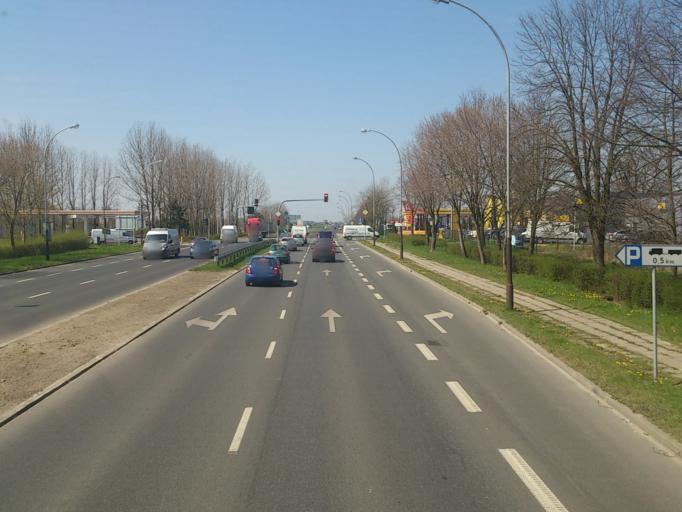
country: PL
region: Lodz Voivodeship
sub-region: Piotrkow Trybunalski
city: Piotrkow Trybunalski
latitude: 51.4074
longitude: 19.6490
